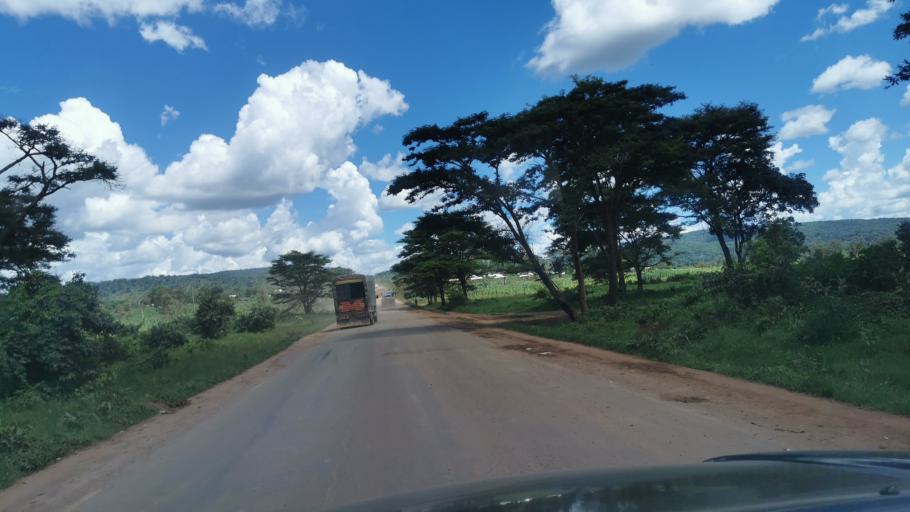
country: TZ
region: Kagera
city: Biharamulo
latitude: -2.8906
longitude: 31.1439
